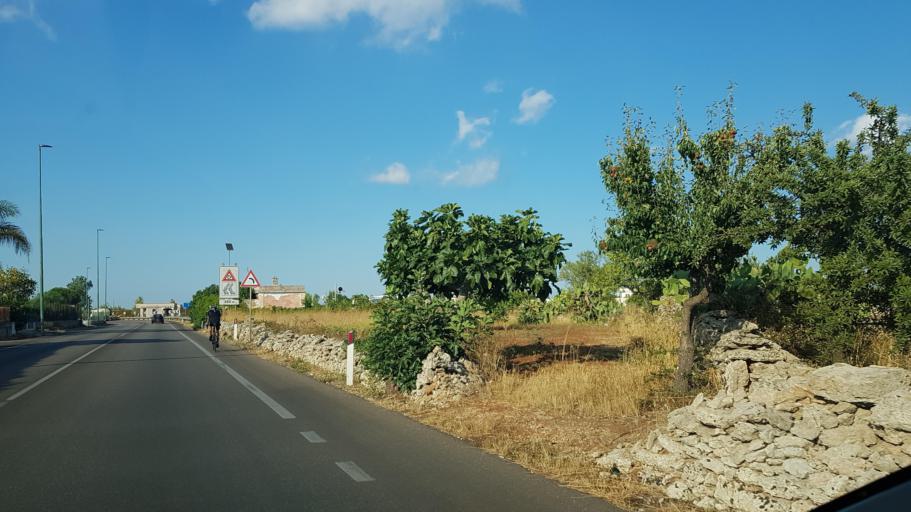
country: IT
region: Apulia
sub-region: Provincia di Lecce
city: Montesano Salentino
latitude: 39.9700
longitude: 18.3250
